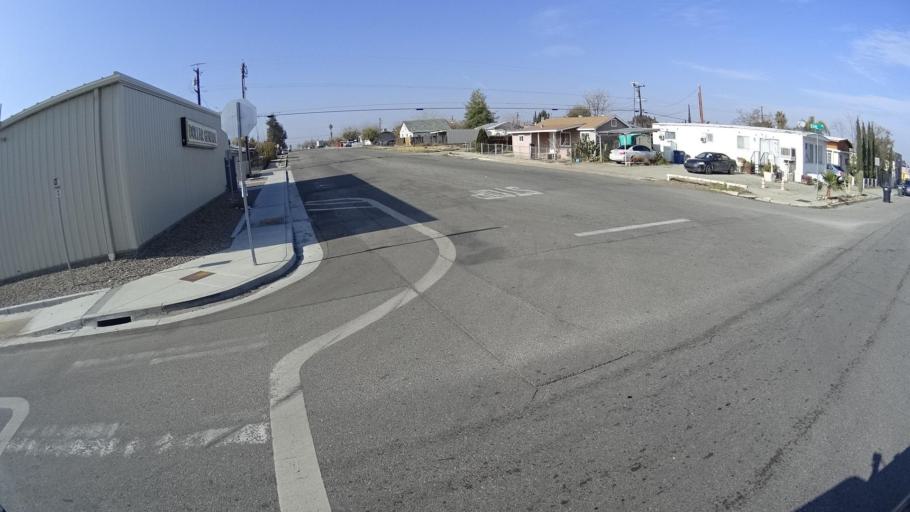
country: US
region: California
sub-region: Kern County
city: Ford City
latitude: 35.1575
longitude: -119.4564
